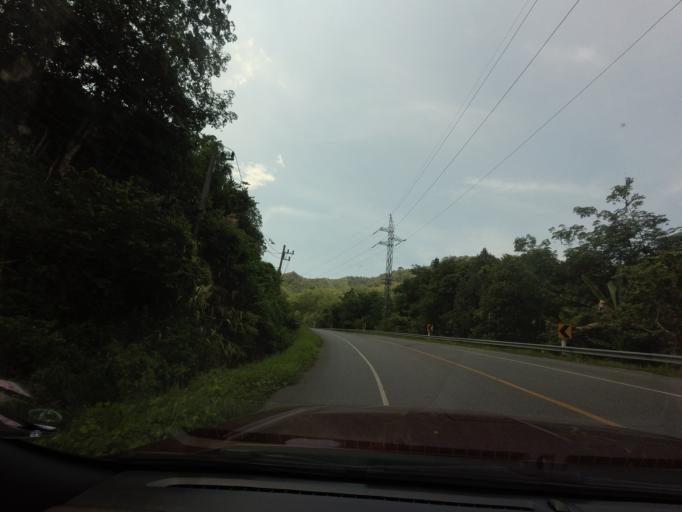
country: TH
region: Yala
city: Than To
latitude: 5.9966
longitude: 101.1915
